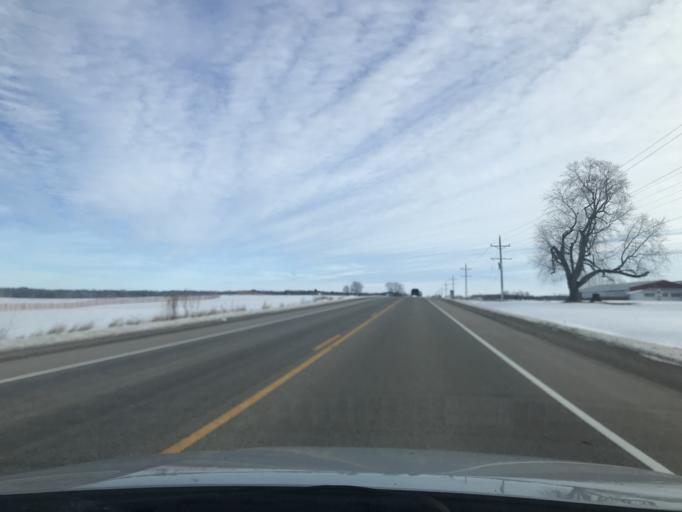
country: US
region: Wisconsin
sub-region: Oconto County
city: Gillett
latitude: 44.8958
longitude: -88.2265
